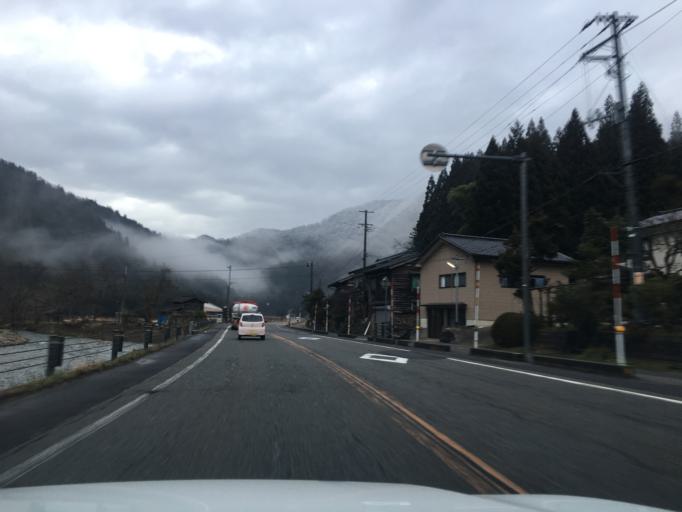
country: JP
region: Niigata
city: Murakami
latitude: 38.4566
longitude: 139.5751
